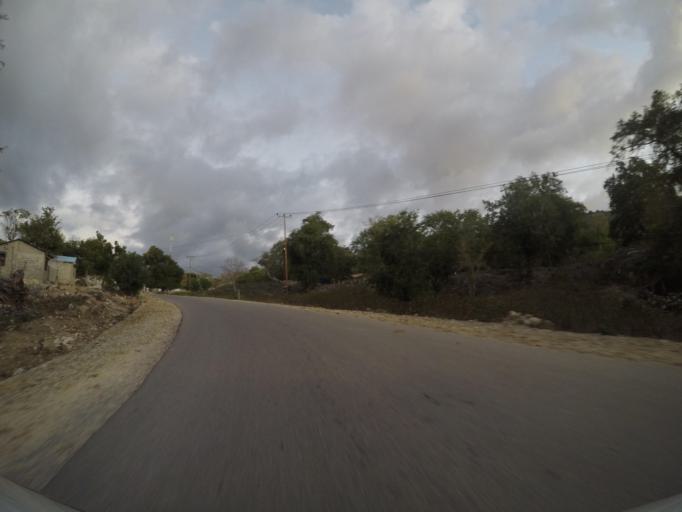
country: TL
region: Lautem
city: Lospalos
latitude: -8.3576
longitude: 127.0558
